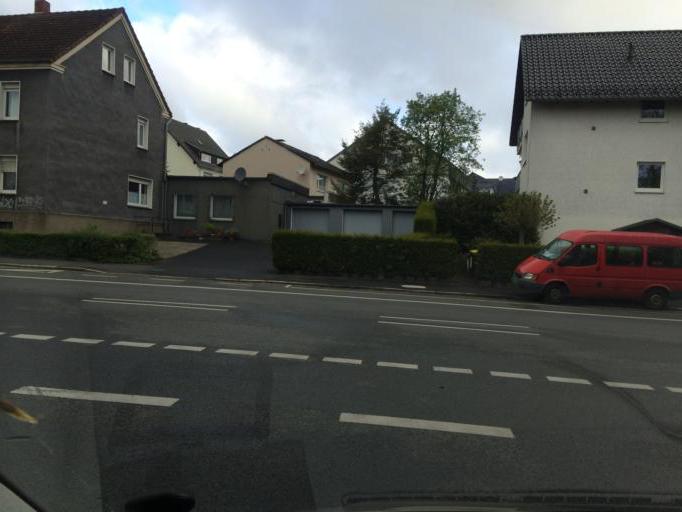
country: DE
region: North Rhine-Westphalia
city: Witten
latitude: 51.4789
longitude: 7.4067
